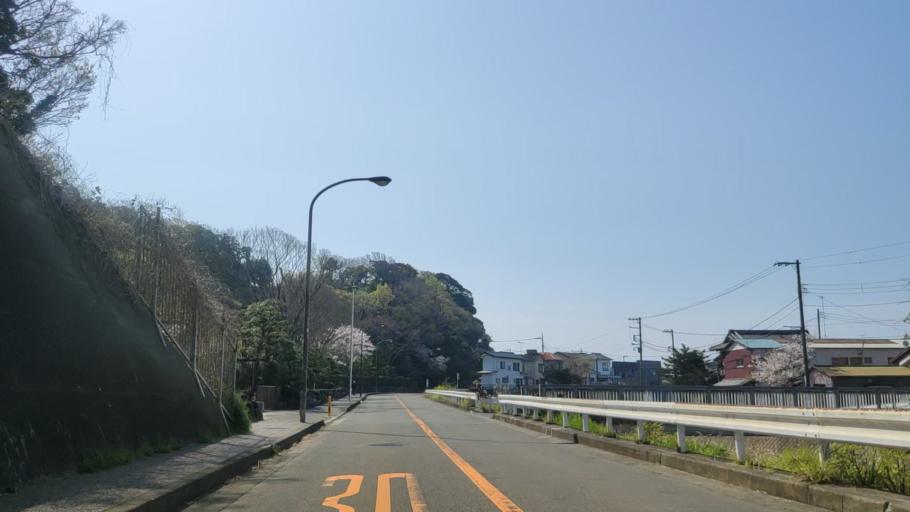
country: JP
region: Kanagawa
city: Oiso
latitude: 35.3069
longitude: 139.2886
